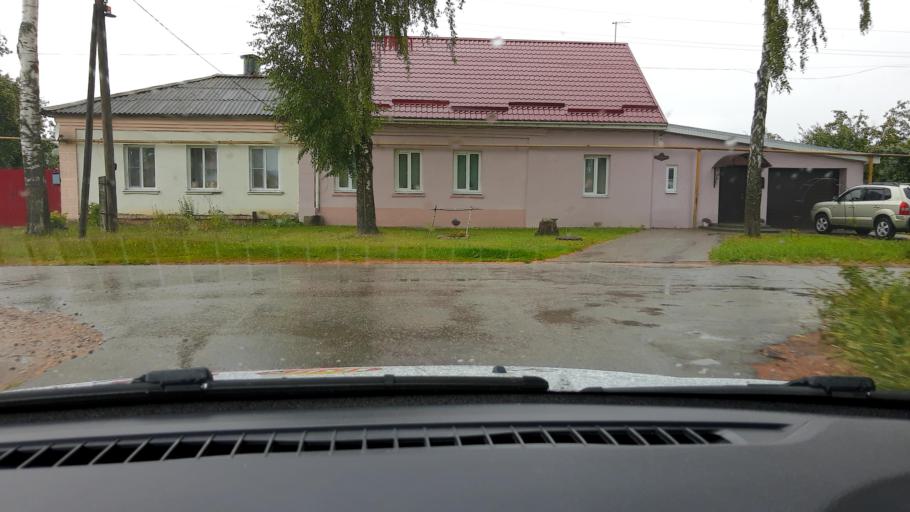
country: RU
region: Nizjnij Novgorod
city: Reshetikha
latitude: 56.1410
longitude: 43.3464
